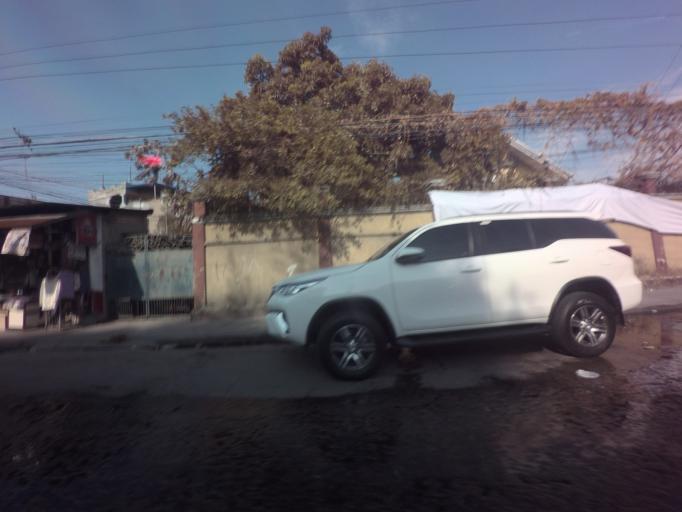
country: PH
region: Calabarzon
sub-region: Province of Rizal
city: Taguig
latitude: 14.4997
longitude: 121.0518
